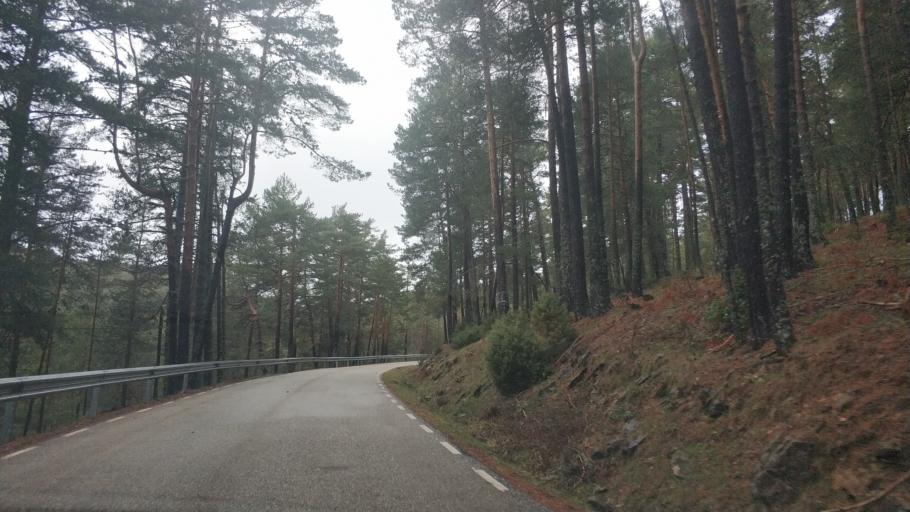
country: ES
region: Castille and Leon
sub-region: Provincia de Burgos
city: Neila
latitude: 42.0405
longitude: -3.0075
